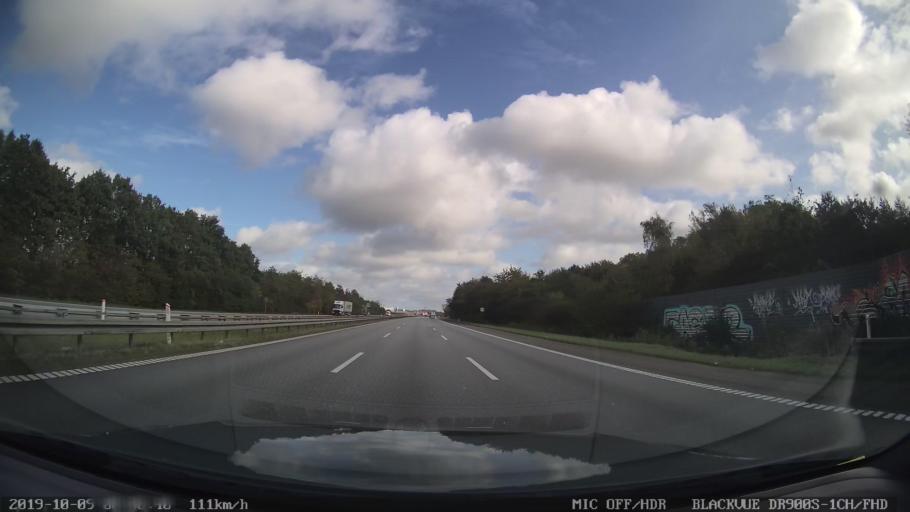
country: DK
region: Capital Region
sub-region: Ishoj Kommune
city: Ishoj
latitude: 55.6142
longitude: 12.3300
